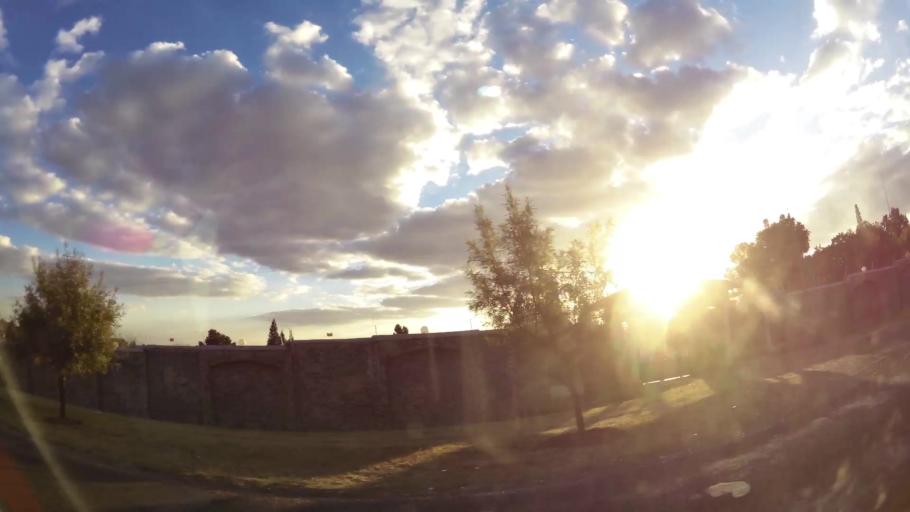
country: ZA
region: Gauteng
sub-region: City of Johannesburg Metropolitan Municipality
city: Midrand
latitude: -25.9623
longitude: 28.1537
